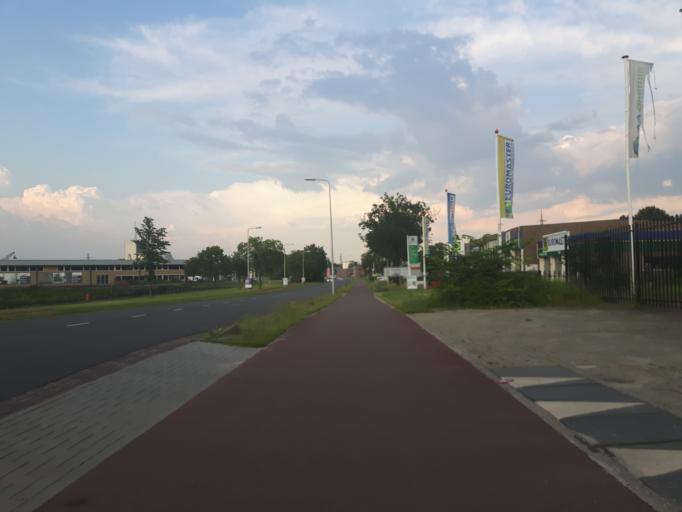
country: NL
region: Overijssel
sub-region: Gemeente Enschede
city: Enschede
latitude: 52.2195
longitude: 6.8518
